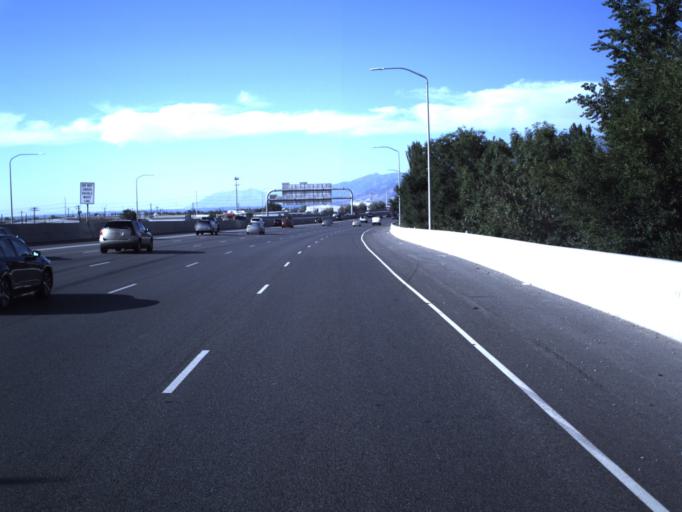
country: US
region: Utah
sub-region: Davis County
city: North Salt Lake
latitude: 40.8423
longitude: -111.9151
